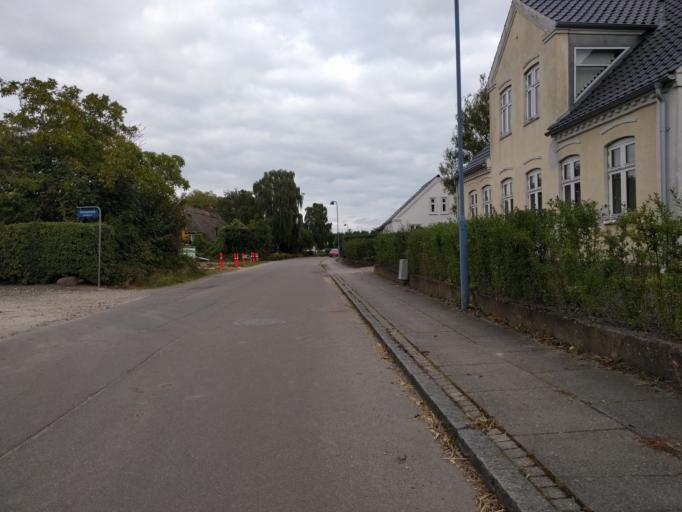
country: DK
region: South Denmark
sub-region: Kerteminde Kommune
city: Munkebo
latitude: 55.4509
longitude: 10.5245
